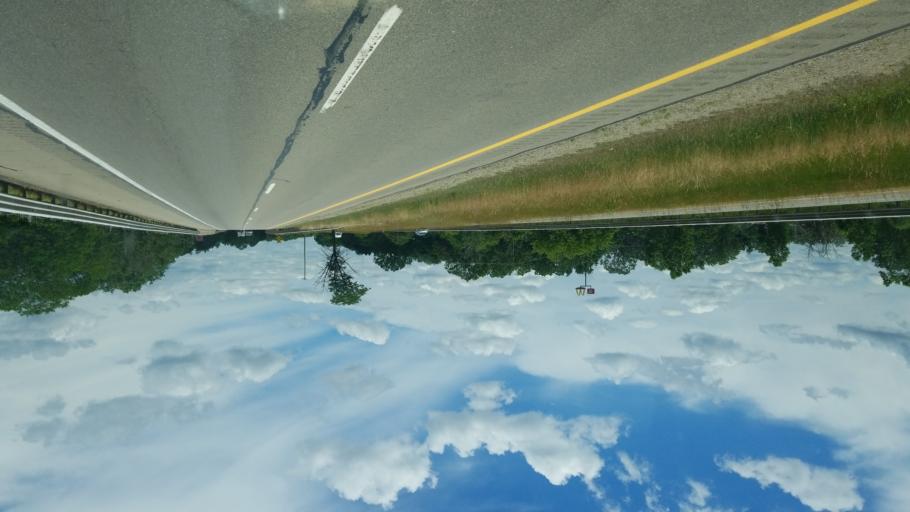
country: US
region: Michigan
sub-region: Eaton County
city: Dimondale
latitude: 42.6646
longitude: -84.5871
